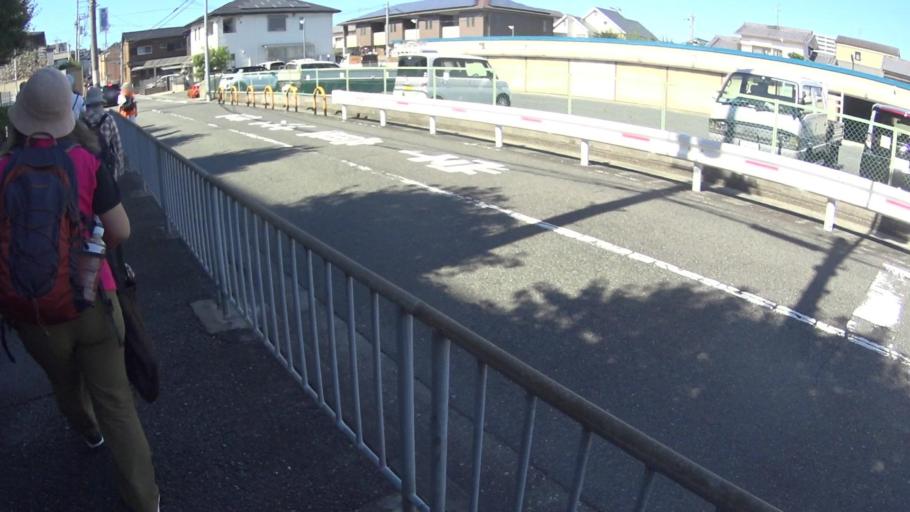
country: JP
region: Osaka
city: Sakai
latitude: 34.5442
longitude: 135.4760
